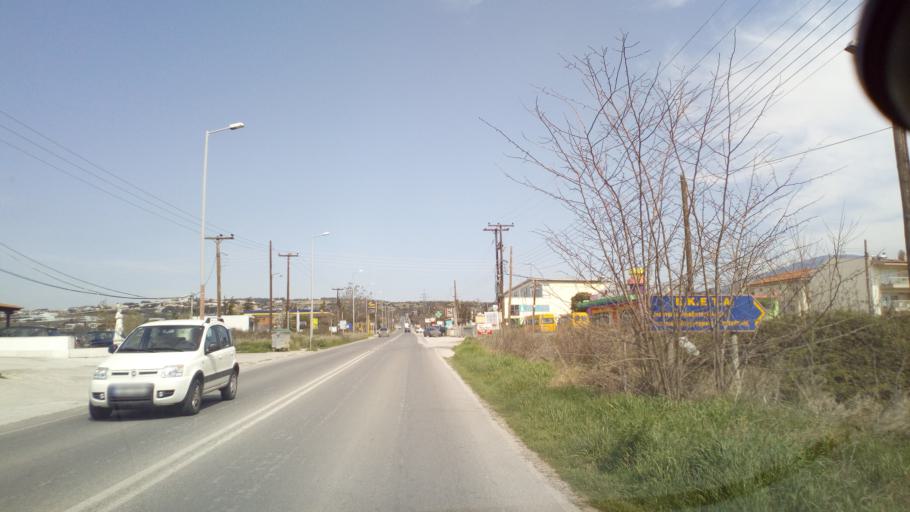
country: GR
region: Central Macedonia
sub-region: Nomos Thessalonikis
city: Thermi
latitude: 40.5572
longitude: 23.0201
